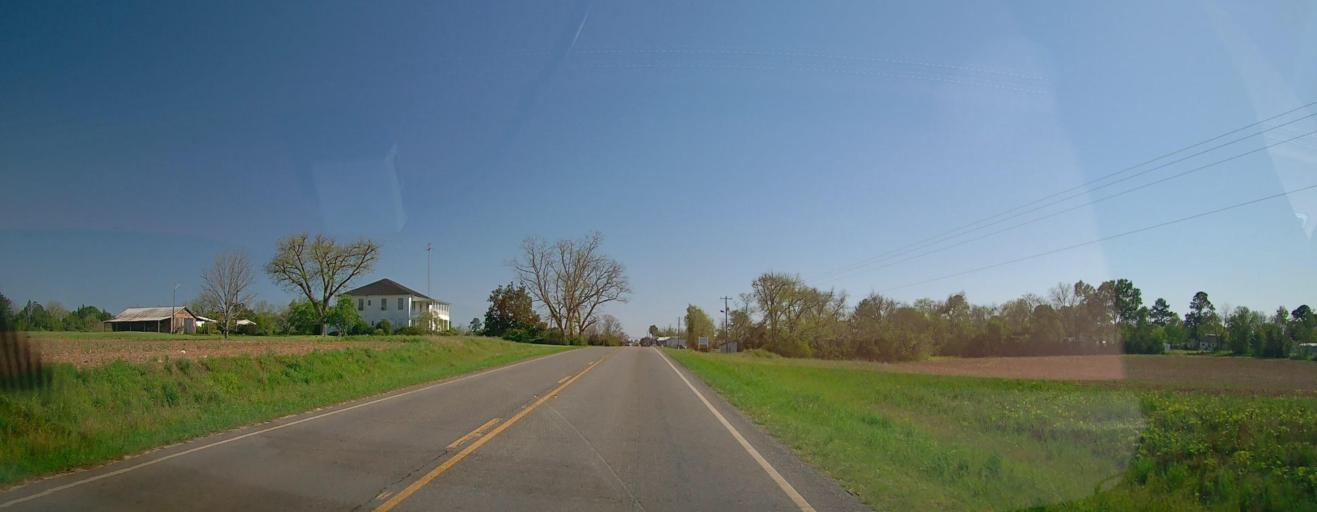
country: US
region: Georgia
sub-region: Wilcox County
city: Rochelle
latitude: 32.1155
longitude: -83.5010
